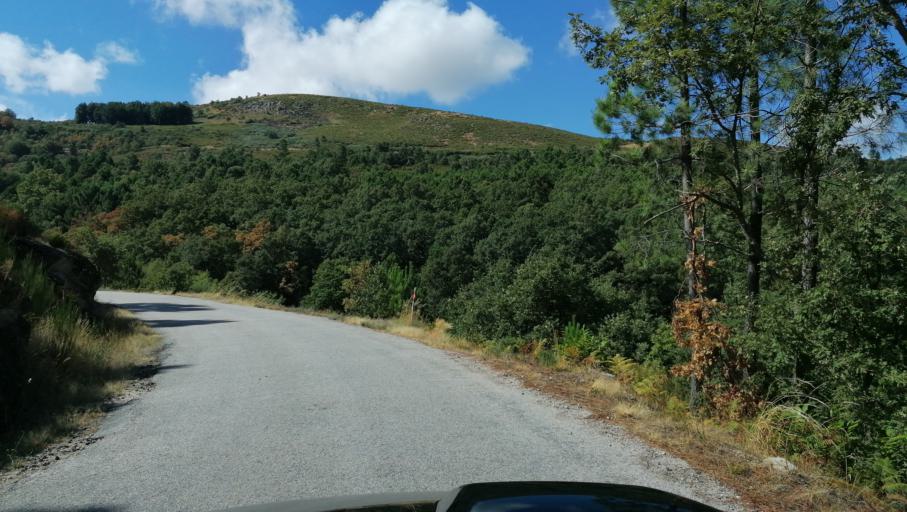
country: PT
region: Vila Real
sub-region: Vila Pouca de Aguiar
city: Vila Pouca de Aguiar
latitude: 41.5565
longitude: -7.6529
